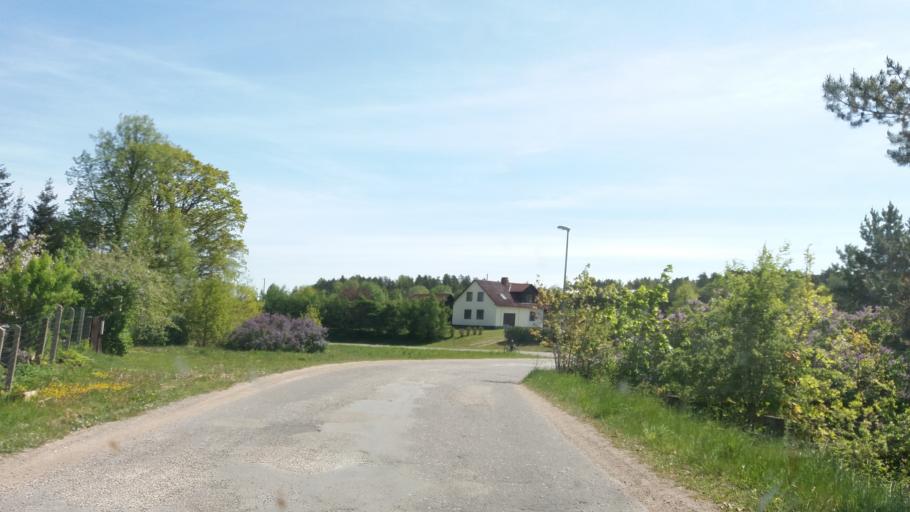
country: LV
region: Talsu Rajons
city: Sabile
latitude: 57.0503
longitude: 22.5801
